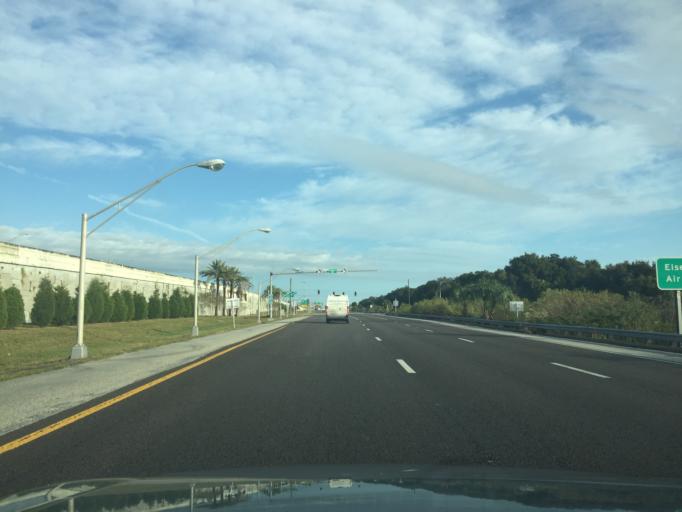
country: US
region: Florida
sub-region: Hillsborough County
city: Town 'n' Country
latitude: 27.9802
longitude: -82.5460
